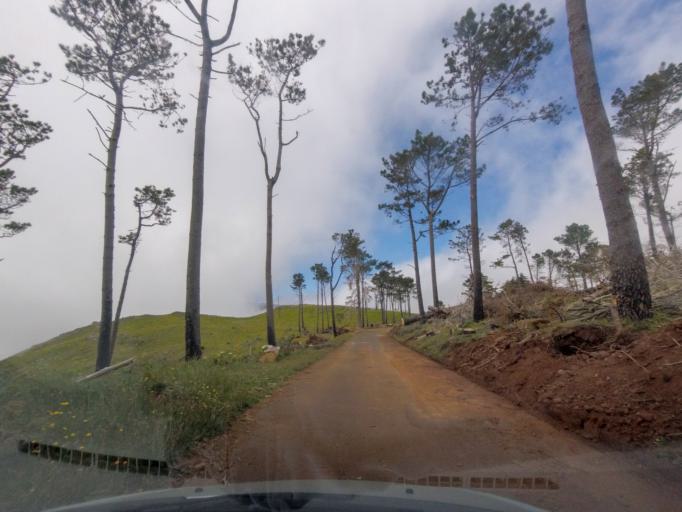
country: PT
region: Madeira
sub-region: Funchal
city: Nossa Senhora do Monte
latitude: 32.7096
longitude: -16.9120
